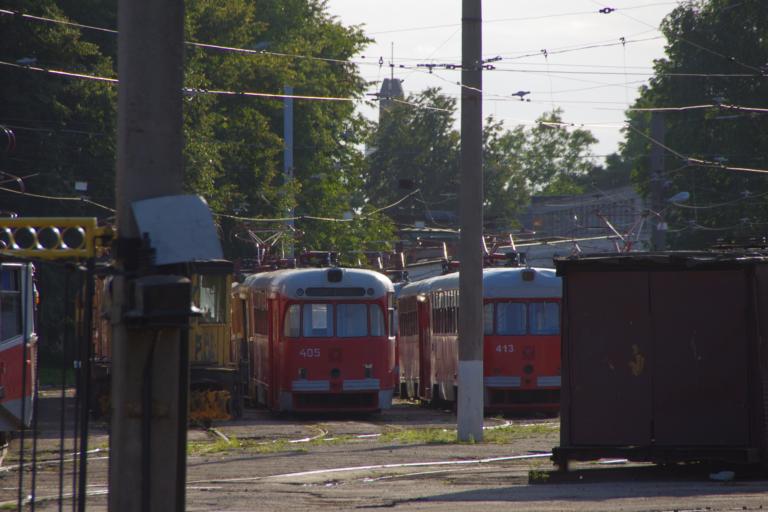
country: BY
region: Vitebsk
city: Vitebsk
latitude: 55.1920
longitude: 30.2287
